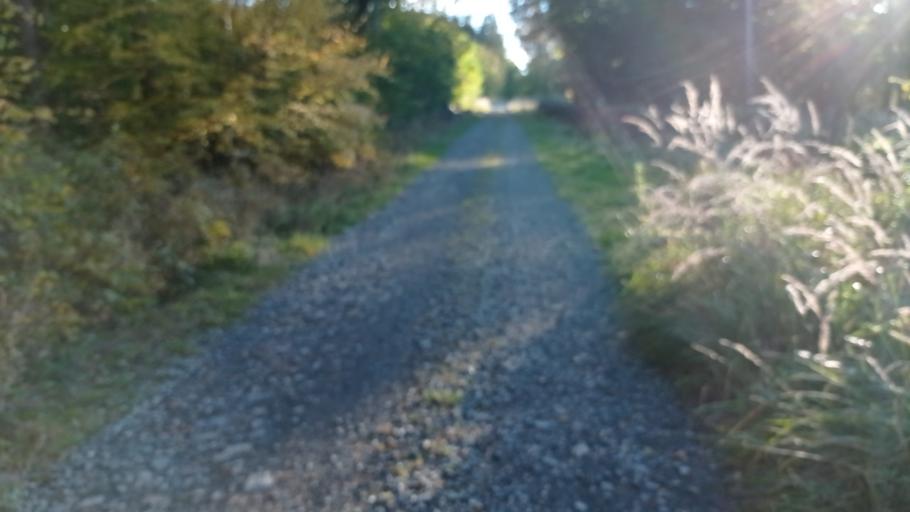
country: CZ
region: Central Bohemia
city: Chynava
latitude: 50.0604
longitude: 14.0557
